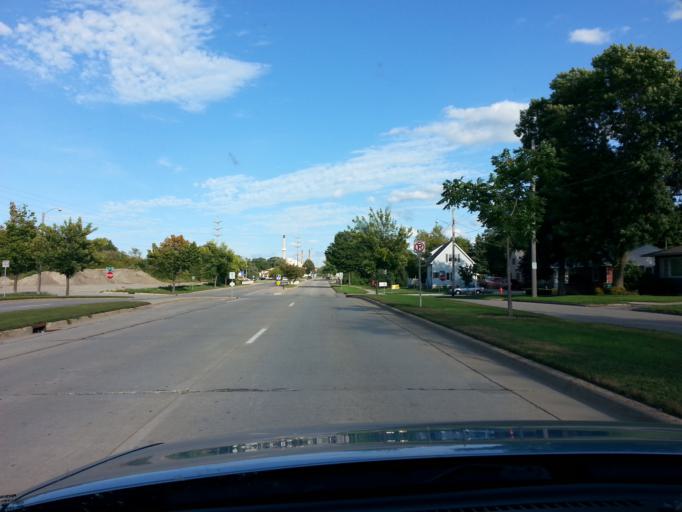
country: US
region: Minnesota
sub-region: Olmsted County
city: Rochester
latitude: 44.0281
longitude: -92.4749
